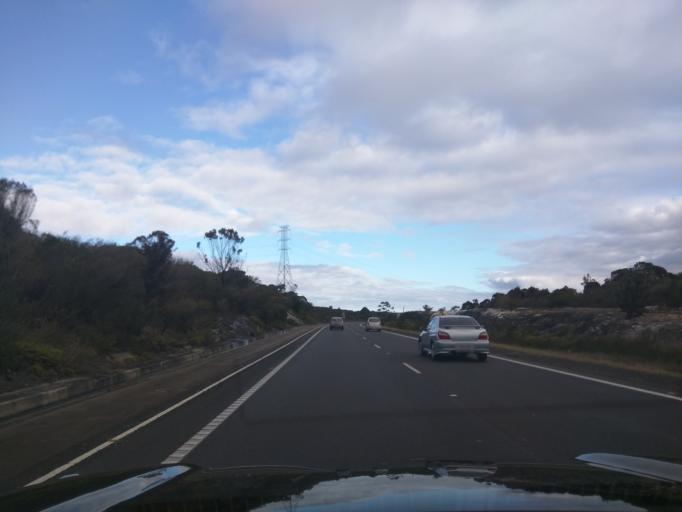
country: AU
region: New South Wales
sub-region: Wollongong
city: Bulli
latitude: -34.2783
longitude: 150.9284
